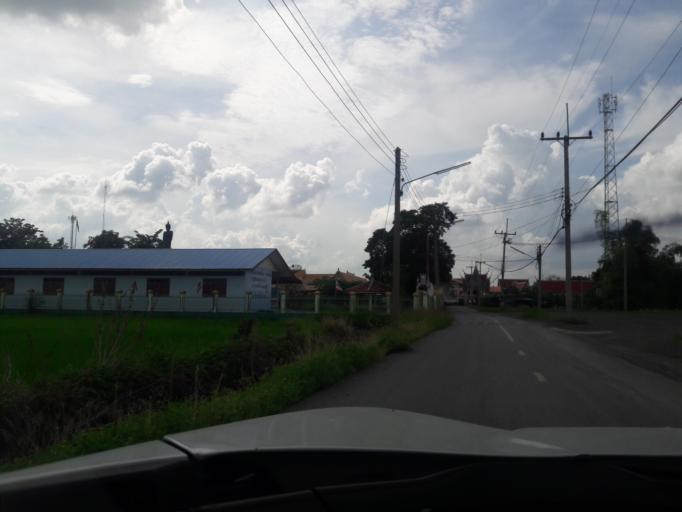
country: TH
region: Lop Buri
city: Ban Mi
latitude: 14.9710
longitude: 100.5262
